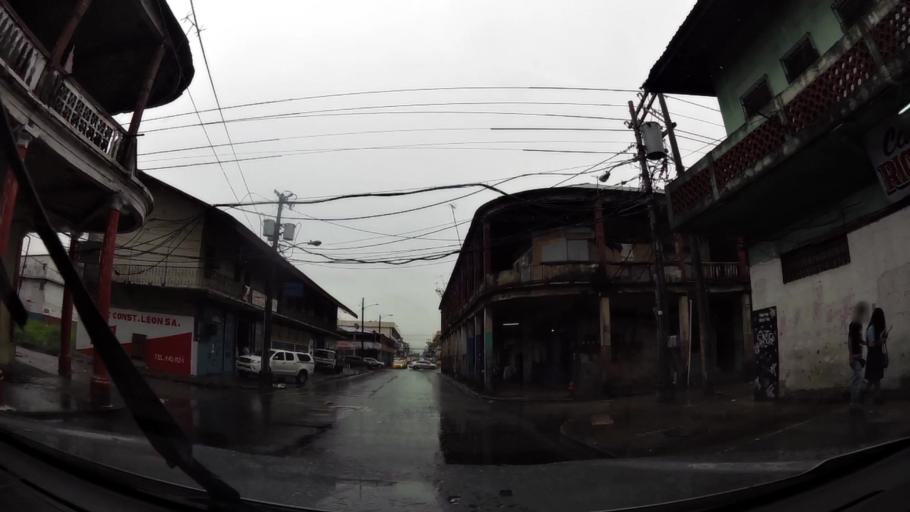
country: PA
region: Colon
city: Colon
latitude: 9.3535
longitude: -79.9023
